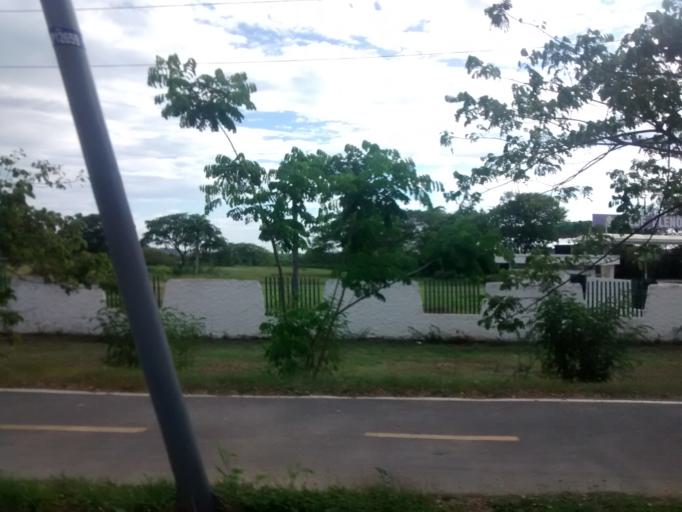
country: CO
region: Cundinamarca
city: Ricaurte
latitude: 4.2919
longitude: -74.7801
